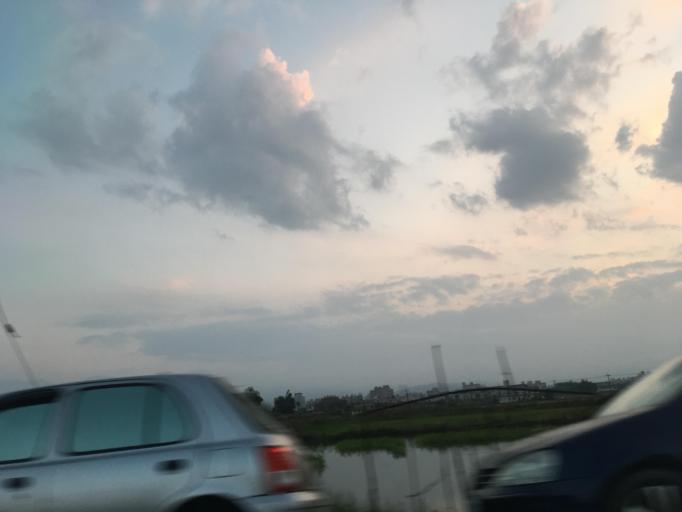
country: TW
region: Taiwan
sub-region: Yilan
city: Yilan
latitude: 24.6918
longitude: 121.7831
